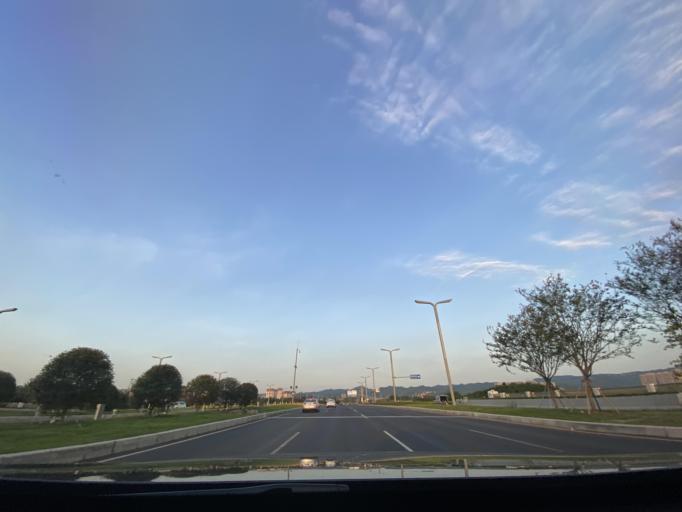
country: CN
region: Sichuan
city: Longquan
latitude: 30.5998
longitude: 104.2667
